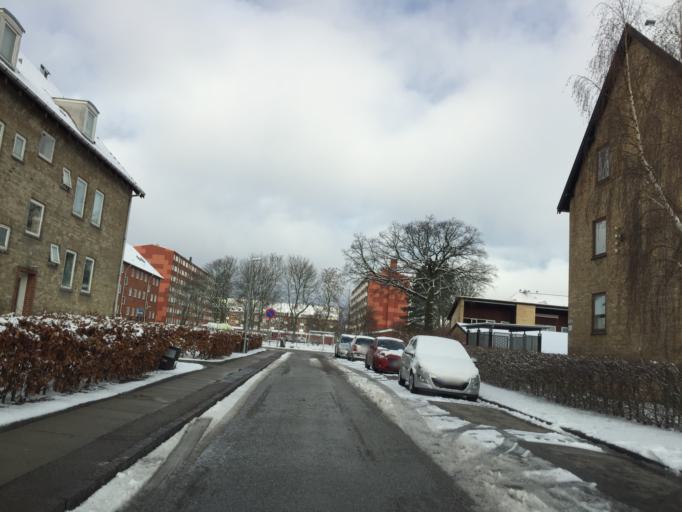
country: DK
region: Capital Region
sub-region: Tarnby Kommune
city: Tarnby
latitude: 55.6336
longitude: 12.6420
